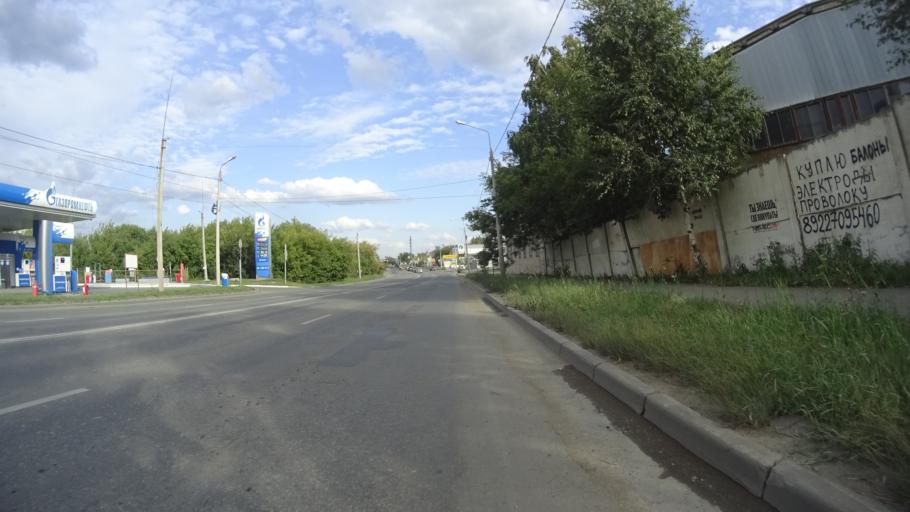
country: RU
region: Chelyabinsk
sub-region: Gorod Chelyabinsk
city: Chelyabinsk
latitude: 55.1978
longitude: 61.3678
